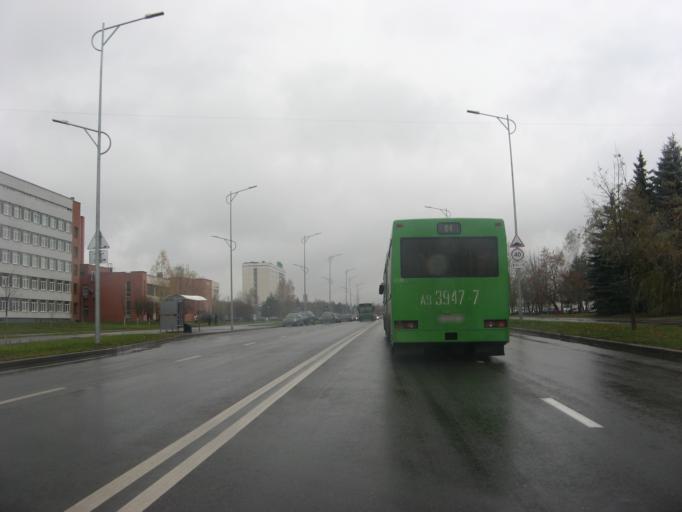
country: BY
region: Minsk
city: Borovlyany
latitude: 53.9276
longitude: 27.6913
